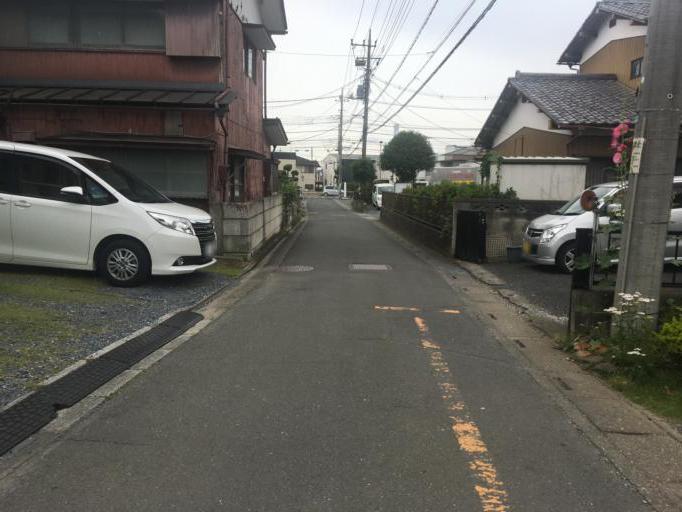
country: JP
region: Saitama
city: Fukiage-fujimi
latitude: 36.0386
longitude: 139.4137
